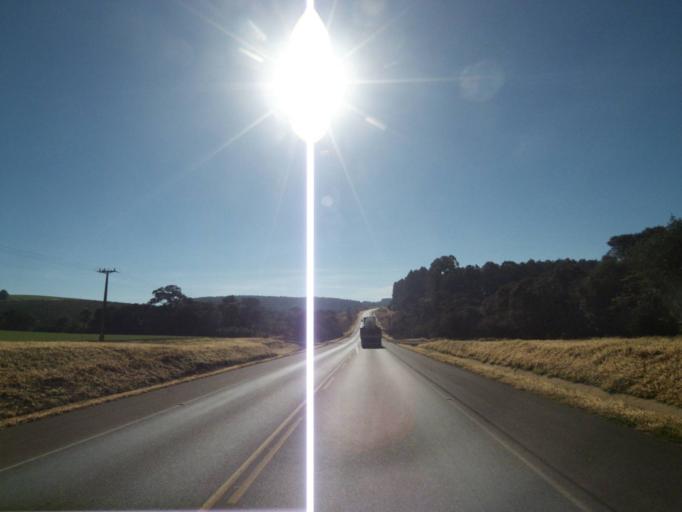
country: BR
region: Parana
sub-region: Tibagi
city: Tibagi
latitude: -24.4700
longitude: -50.4432
